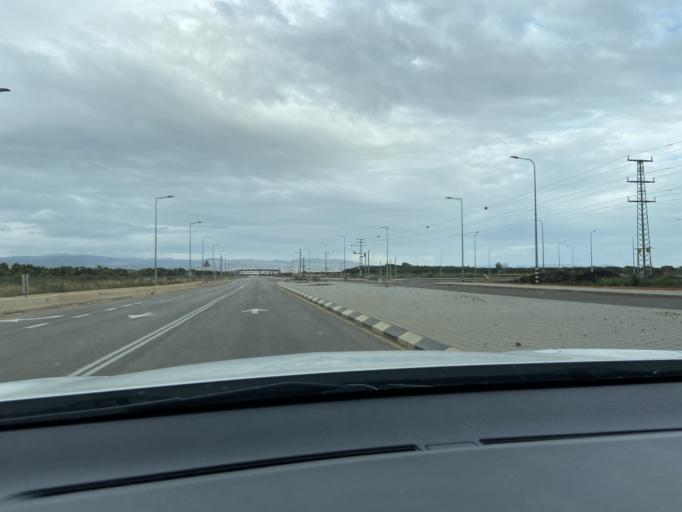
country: IL
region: Northern District
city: El Mazra`a
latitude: 32.9794
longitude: 35.1074
